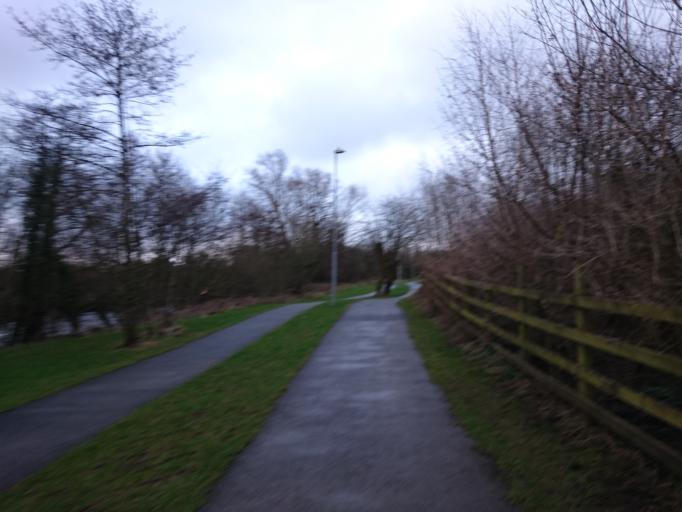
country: IE
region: Leinster
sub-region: Kilkenny
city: Kilkenny
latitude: 52.6676
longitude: -7.2598
